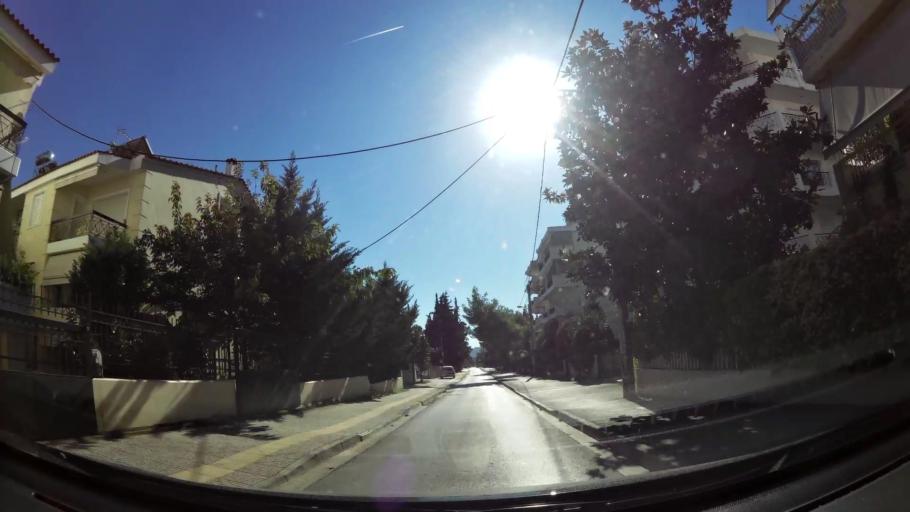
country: GR
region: Attica
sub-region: Nomarchia Athinas
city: Vrilissia
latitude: 38.0330
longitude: 23.8394
